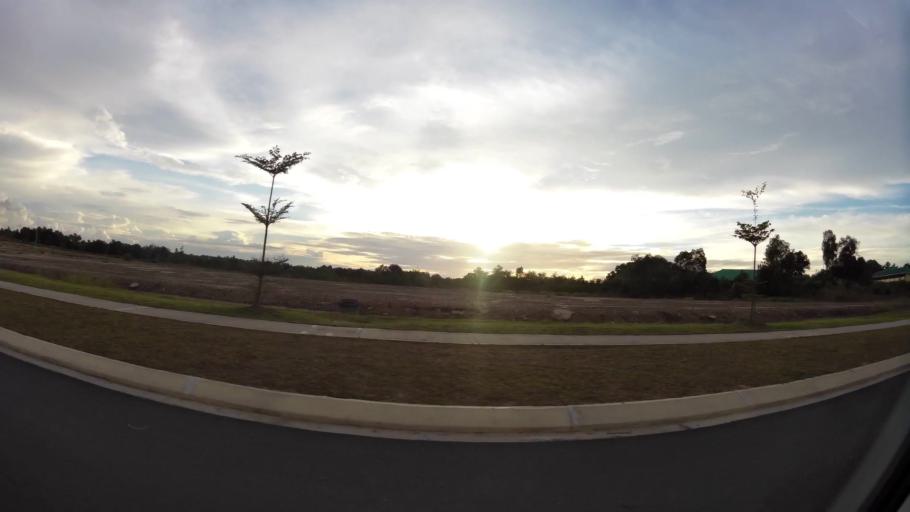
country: BN
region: Brunei and Muara
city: Bandar Seri Begawan
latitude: 4.9902
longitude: 114.9829
